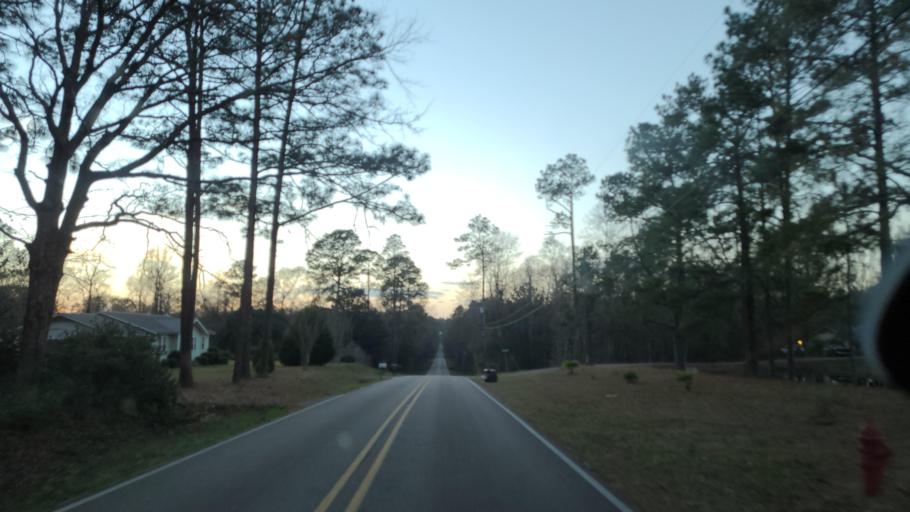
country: US
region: Mississippi
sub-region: Forrest County
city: Hattiesburg
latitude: 31.1675
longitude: -89.2321
